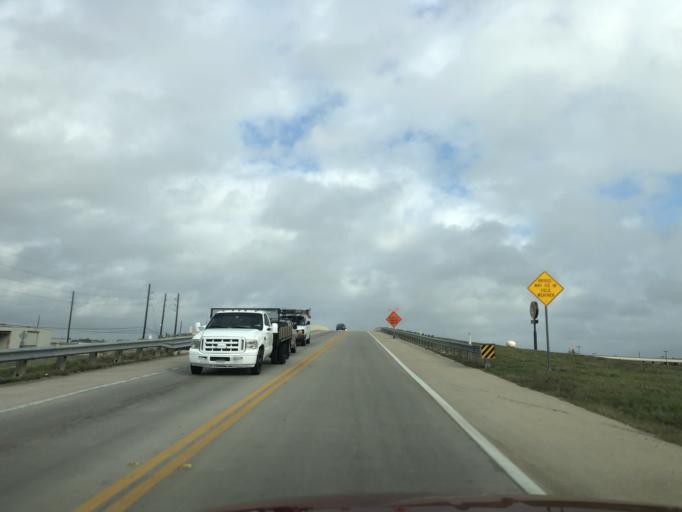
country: US
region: Texas
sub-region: Harris County
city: Katy
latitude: 29.7755
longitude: -95.8501
